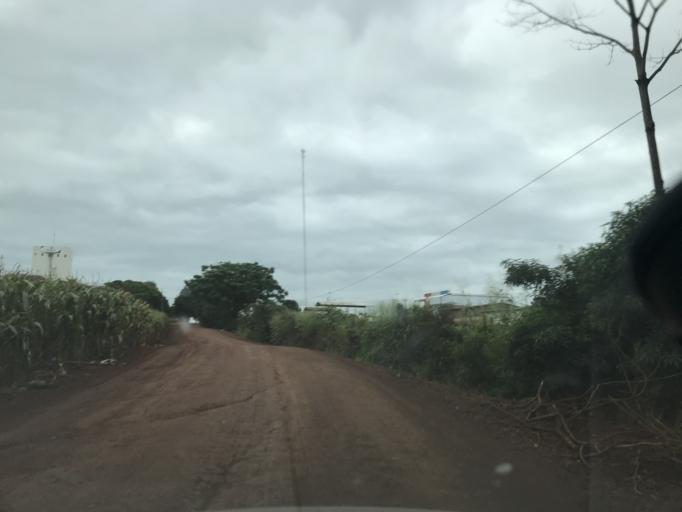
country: BR
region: Parana
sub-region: Palotina
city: Palotina
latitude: -24.3040
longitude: -53.8311
